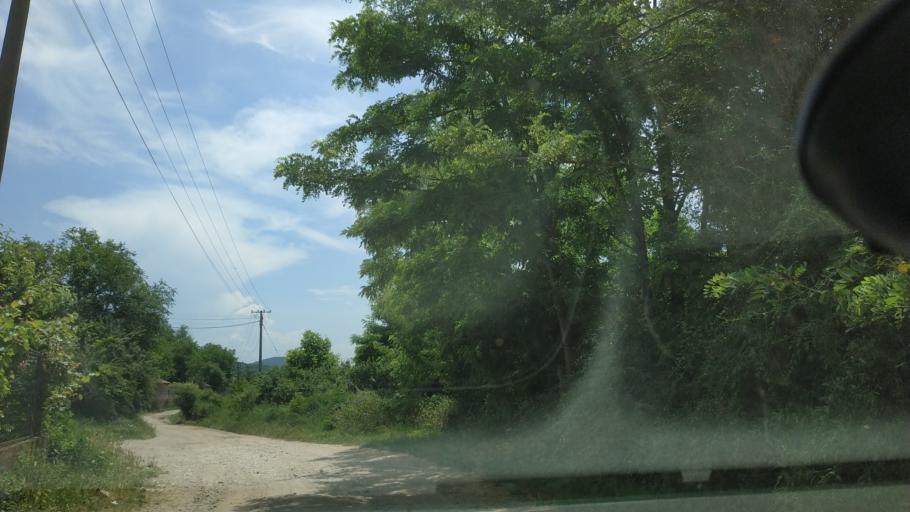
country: RS
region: Central Serbia
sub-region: Nisavski Okrug
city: Aleksinac
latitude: 43.5764
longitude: 21.7016
